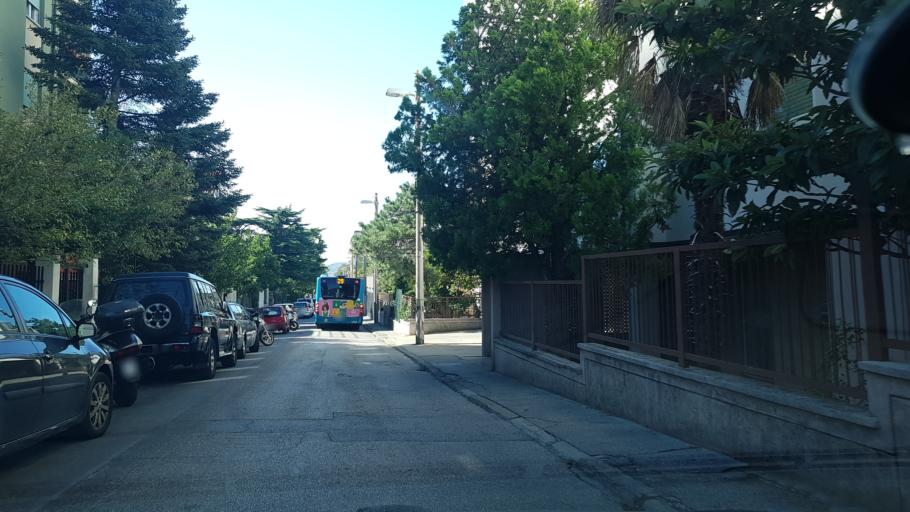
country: IT
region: Friuli Venezia Giulia
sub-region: Provincia di Trieste
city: Trieste
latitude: 45.6284
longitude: 13.7893
